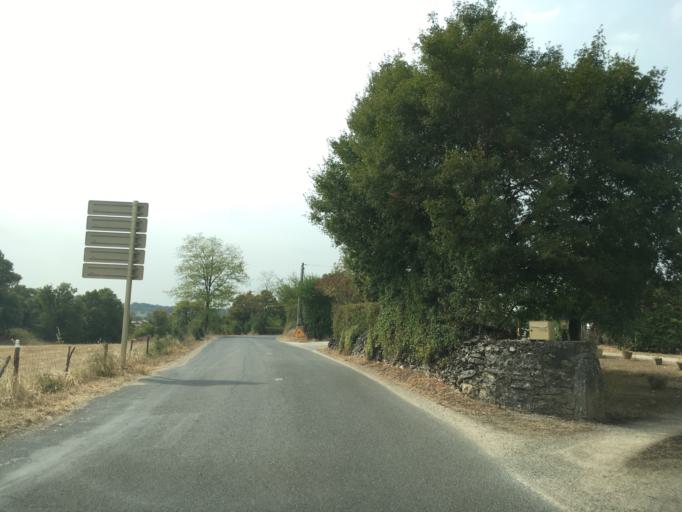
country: FR
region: Midi-Pyrenees
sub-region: Departement du Lot
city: Gramat
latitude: 44.8061
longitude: 1.6239
